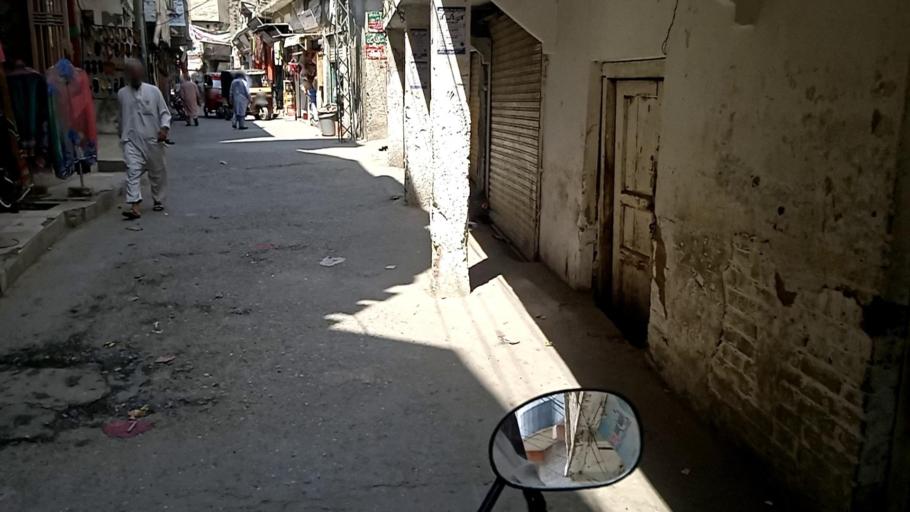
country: PK
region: Khyber Pakhtunkhwa
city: Mingora
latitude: 34.7758
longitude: 72.3540
